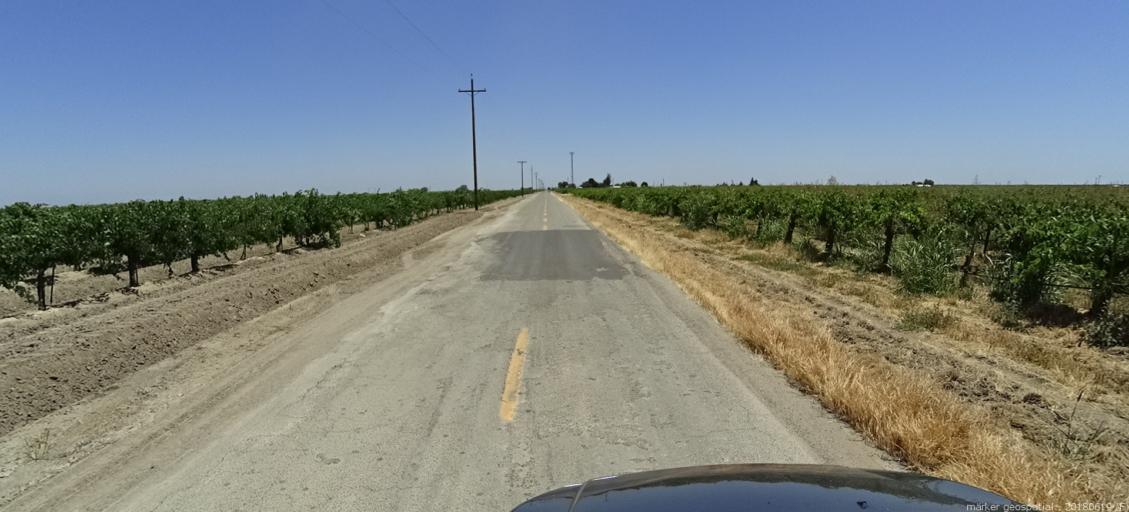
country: US
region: California
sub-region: Madera County
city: Parkwood
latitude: 36.8585
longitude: -120.1369
